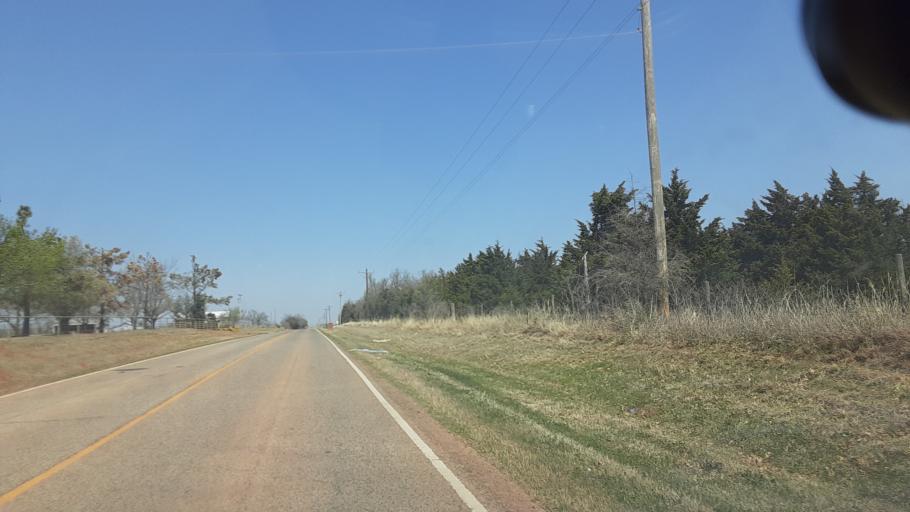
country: US
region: Oklahoma
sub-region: Logan County
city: Guthrie
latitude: 35.8239
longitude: -97.4784
